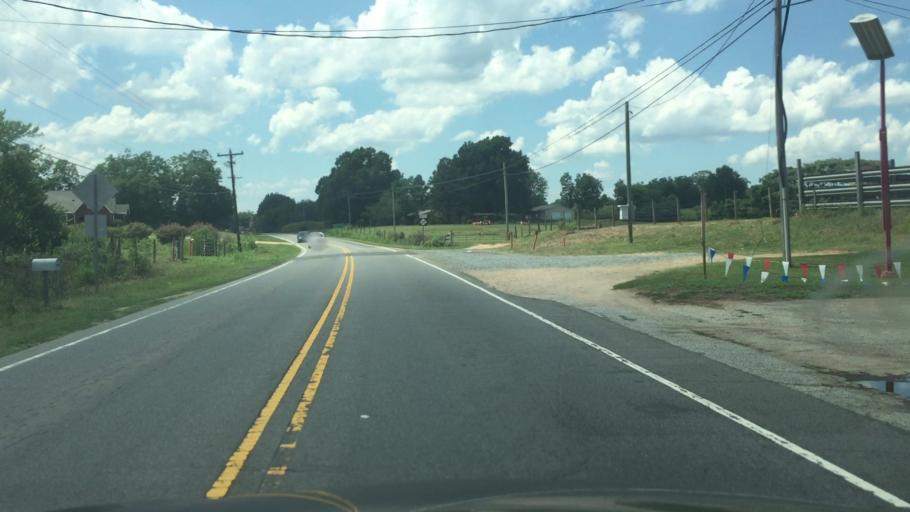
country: US
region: North Carolina
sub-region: Rowan County
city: Enochville
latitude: 35.5716
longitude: -80.6549
